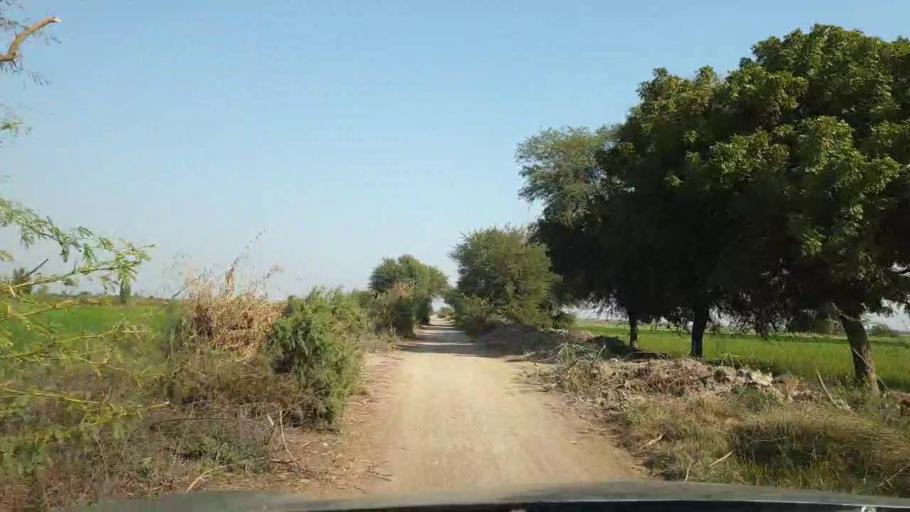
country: PK
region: Sindh
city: Berani
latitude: 25.6223
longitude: 68.8326
